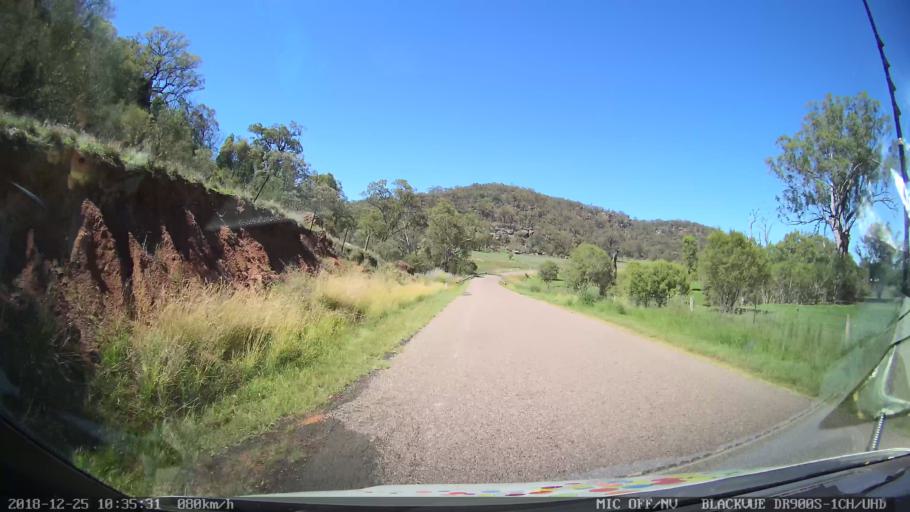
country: AU
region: New South Wales
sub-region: Upper Hunter Shire
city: Merriwa
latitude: -32.3994
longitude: 150.3955
